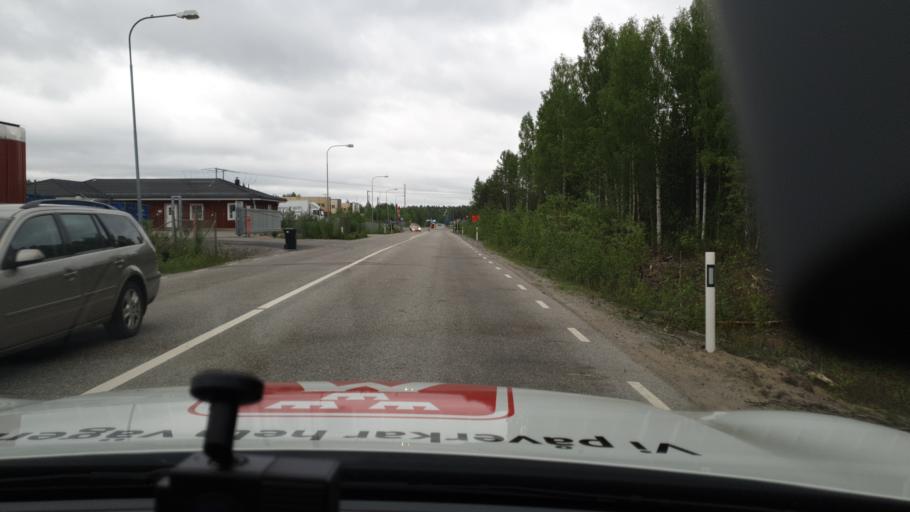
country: SE
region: Vaesterbotten
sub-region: Umea Kommun
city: Roback
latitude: 63.8483
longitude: 20.1417
